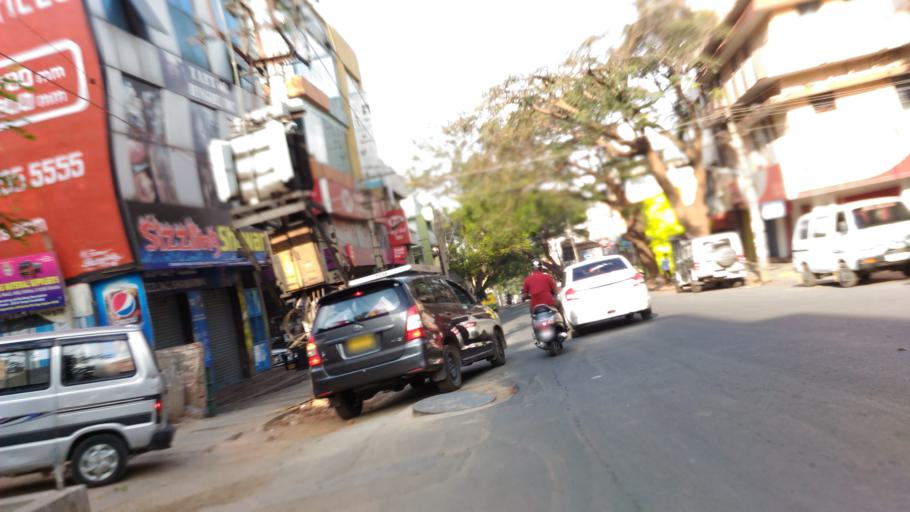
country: IN
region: Karnataka
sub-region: Bangalore Urban
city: Bangalore
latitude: 12.9420
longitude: 77.5520
